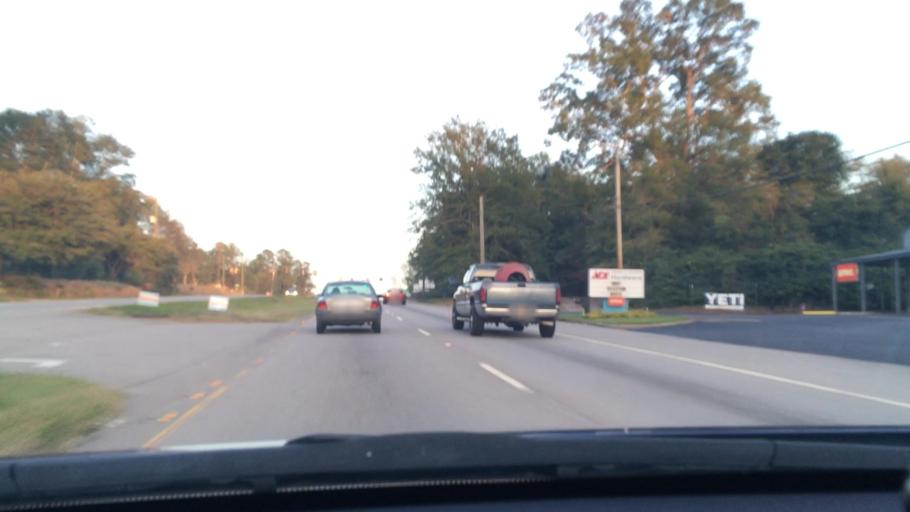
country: US
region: South Carolina
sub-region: Richland County
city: Hopkins
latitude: 33.9513
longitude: -80.8449
